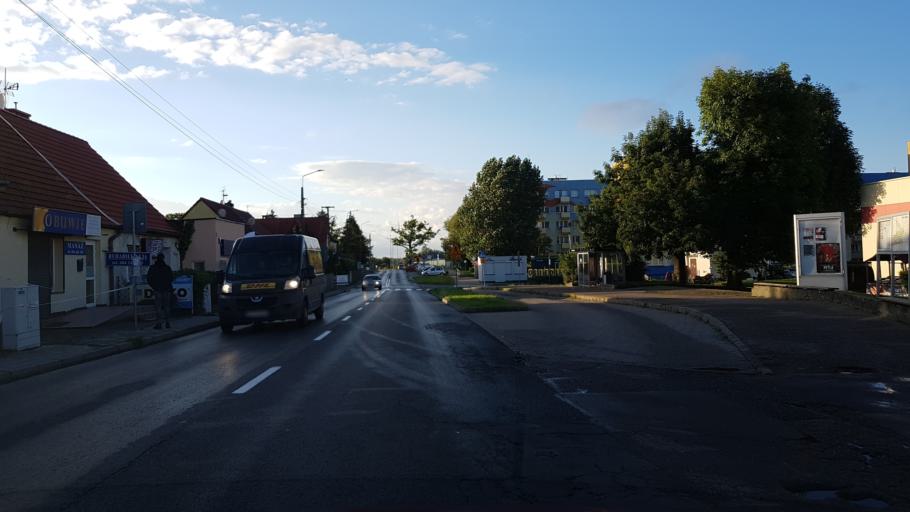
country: PL
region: West Pomeranian Voivodeship
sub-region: Koszalin
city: Koszalin
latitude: 54.2062
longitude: 16.1626
